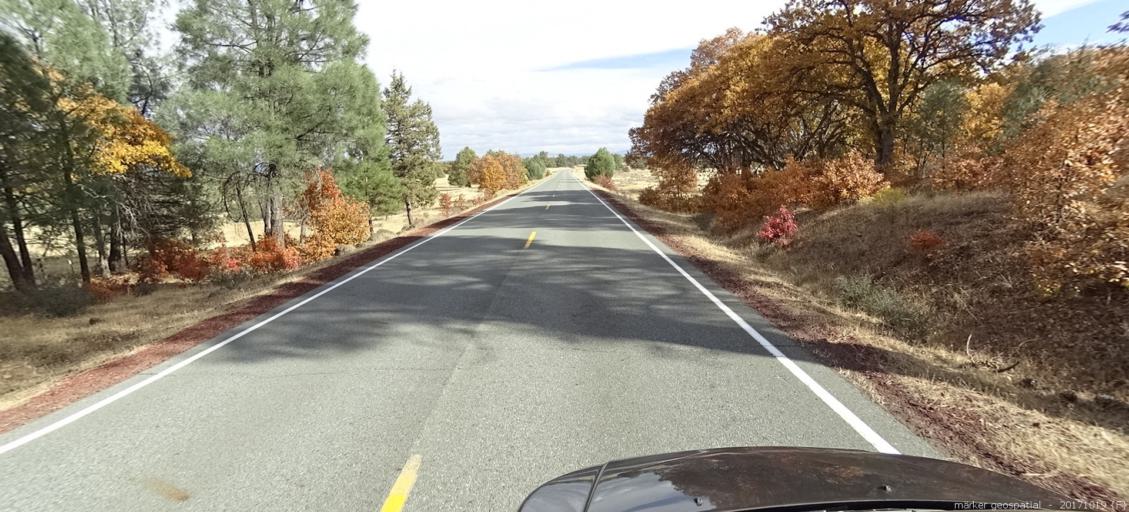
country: US
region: California
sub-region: Shasta County
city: Burney
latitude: 41.0086
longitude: -121.4624
